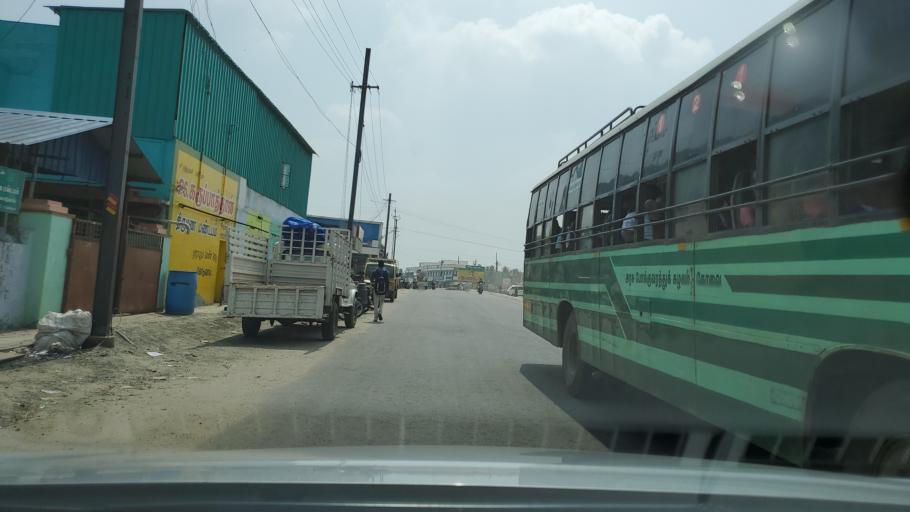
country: IN
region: Tamil Nadu
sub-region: Tiruppur
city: Kangayam
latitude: 10.9409
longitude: 77.4389
